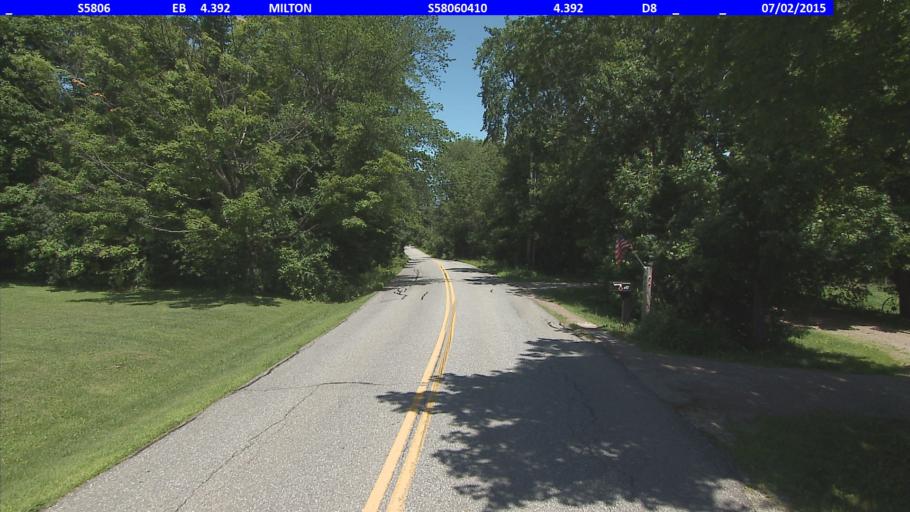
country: US
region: Vermont
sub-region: Chittenden County
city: Milton
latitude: 44.6841
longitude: -73.1763
